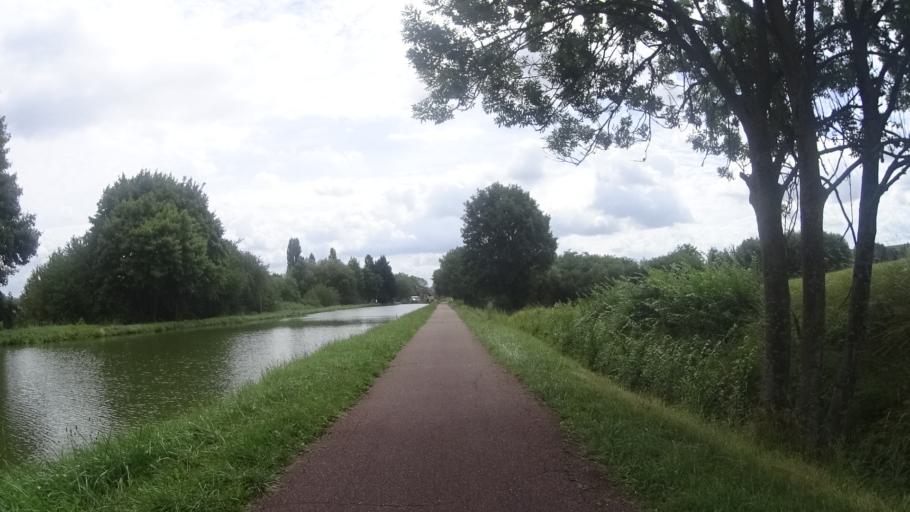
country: FR
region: Alsace
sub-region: Departement du Bas-Rhin
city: Dettwiller
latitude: 48.7444
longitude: 7.4717
